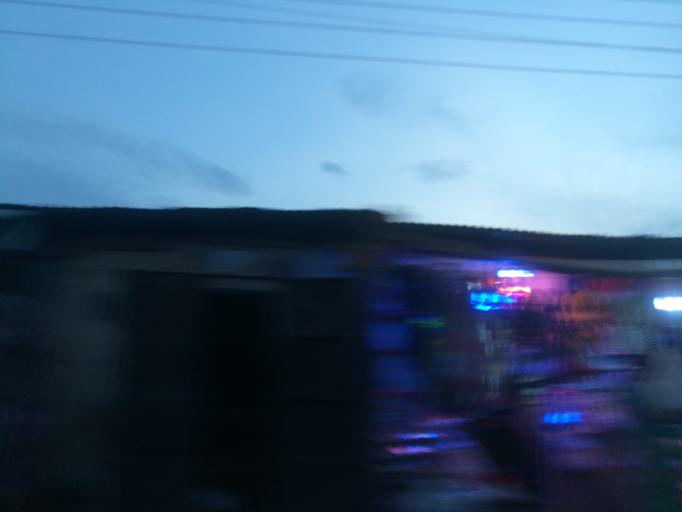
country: NG
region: Oyo
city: Ibadan
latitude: 7.3720
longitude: 3.9037
